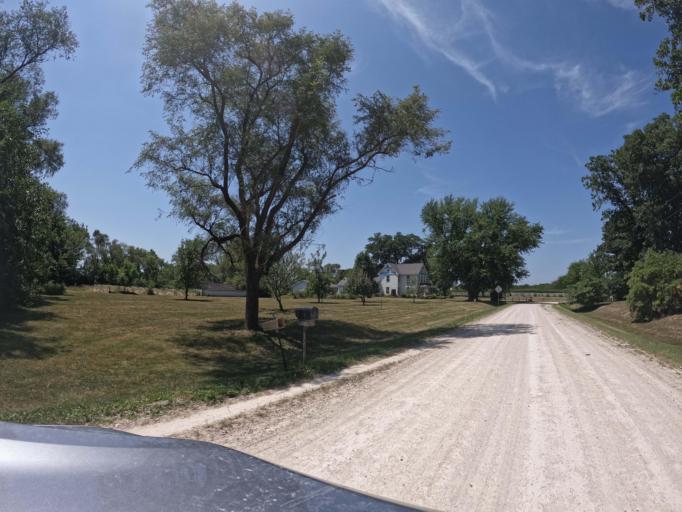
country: US
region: Iowa
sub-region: Henry County
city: Mount Pleasant
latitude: 40.9120
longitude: -91.5490
